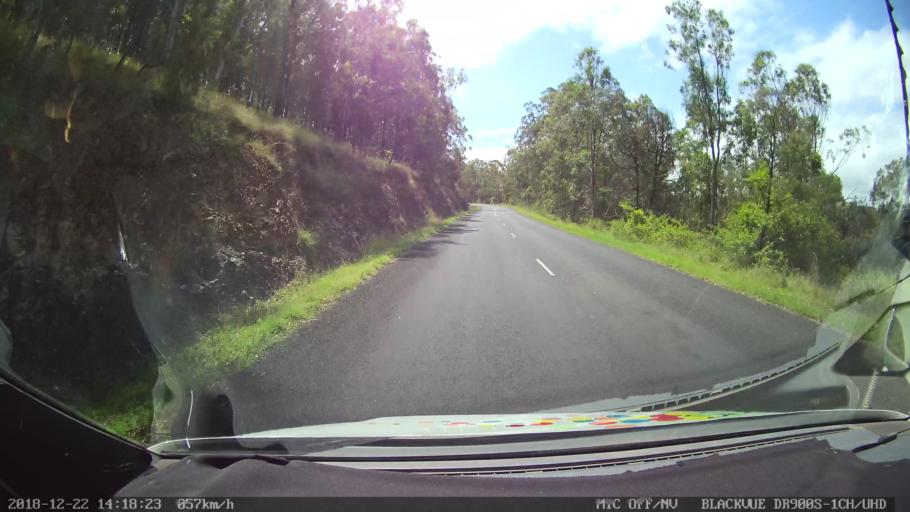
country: AU
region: New South Wales
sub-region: Clarence Valley
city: Coutts Crossing
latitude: -30.0078
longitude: 152.6645
